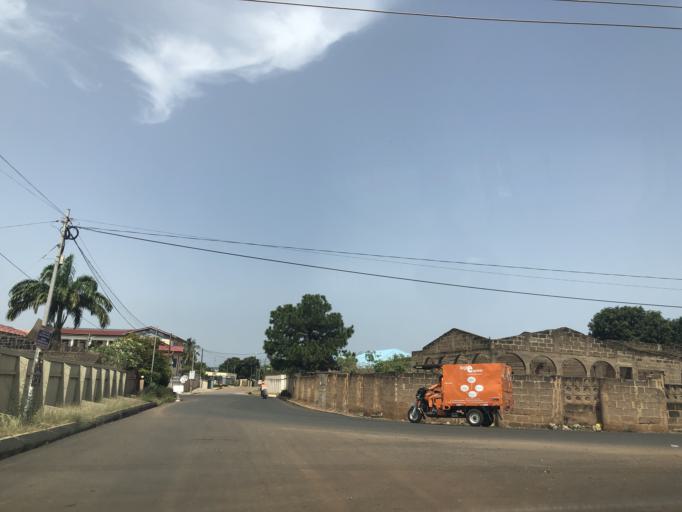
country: GH
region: Greater Accra
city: Dome
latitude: 5.6209
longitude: -0.2499
